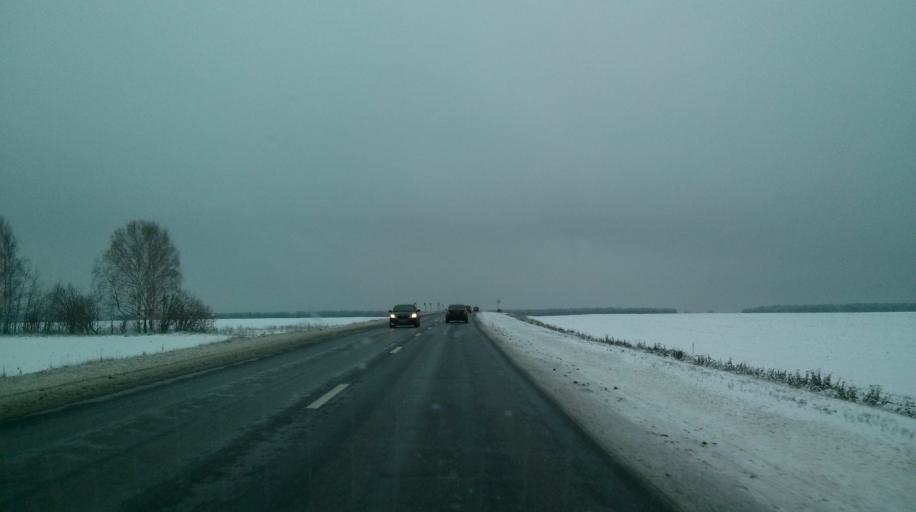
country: RU
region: Nizjnij Novgorod
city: Bogorodsk
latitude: 56.0926
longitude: 43.5754
